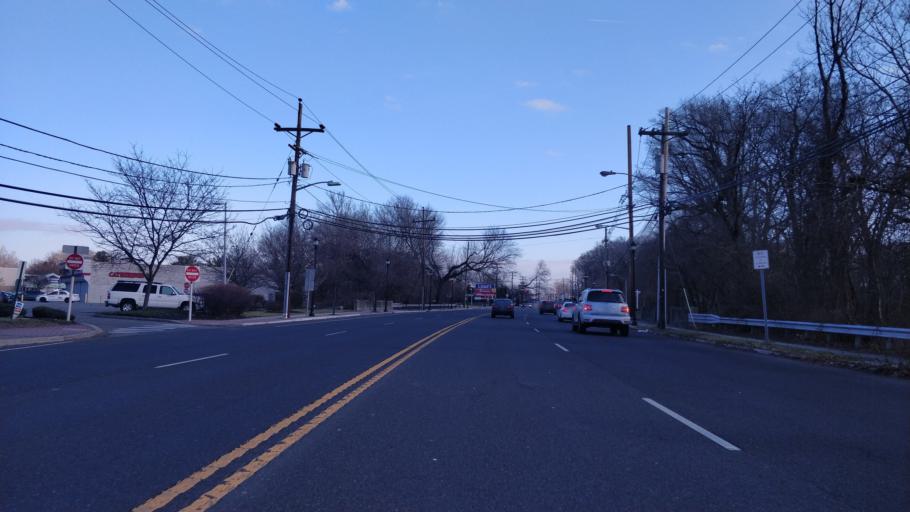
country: US
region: New Jersey
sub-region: Union County
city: Union
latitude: 40.6937
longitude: -74.2582
